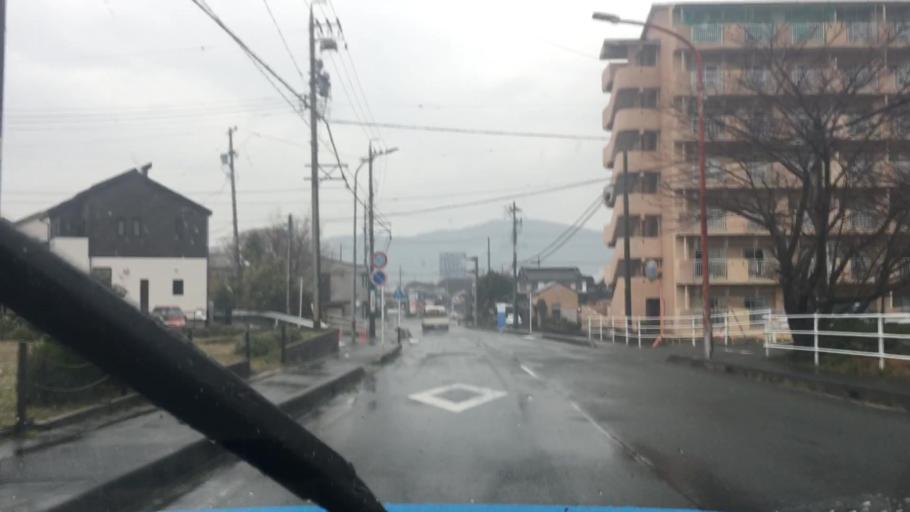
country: JP
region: Aichi
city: Tahara
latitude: 34.6611
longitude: 137.2787
